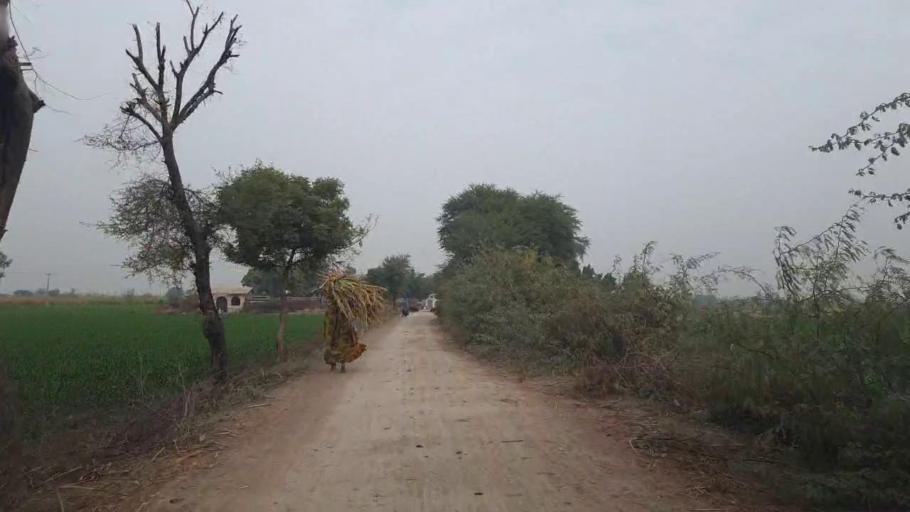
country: PK
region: Sindh
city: Tando Adam
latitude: 25.7289
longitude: 68.7385
